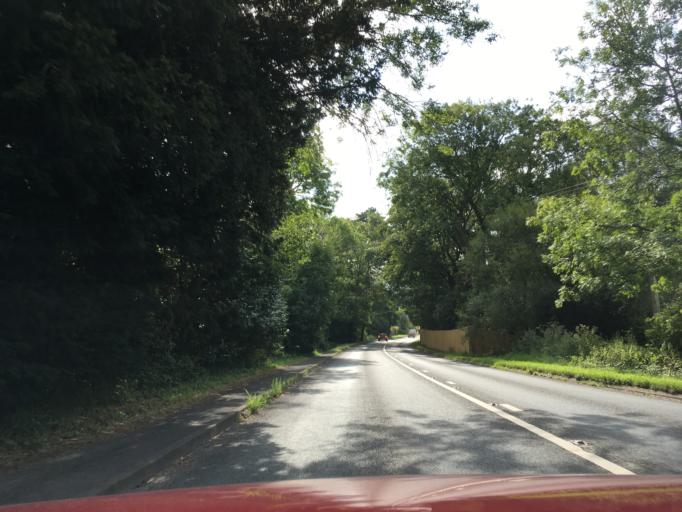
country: GB
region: England
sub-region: Hampshire
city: Bishops Waltham
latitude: 50.9670
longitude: -1.2438
